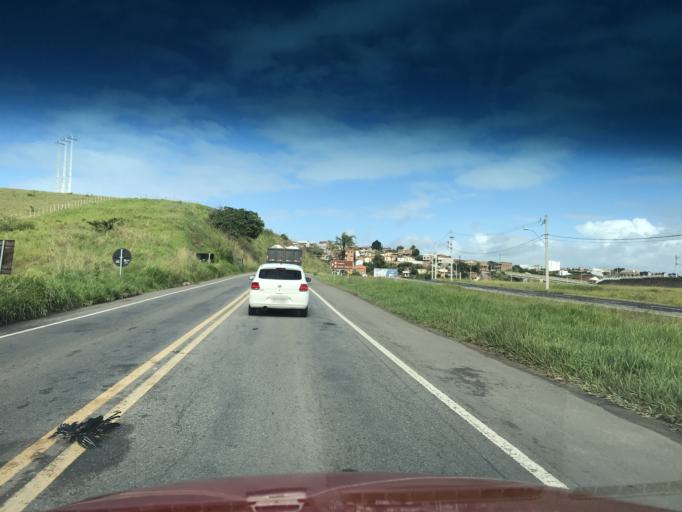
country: BR
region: Bahia
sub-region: Santo Antonio De Jesus
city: Santo Antonio de Jesus
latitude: -12.9539
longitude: -39.2563
